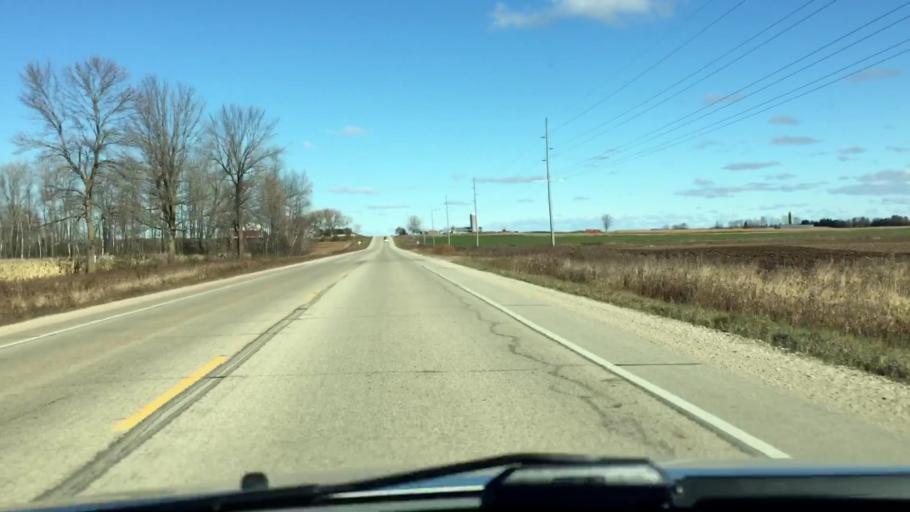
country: US
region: Wisconsin
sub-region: Oconto County
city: Gillett
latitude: 44.8584
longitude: -88.2479
